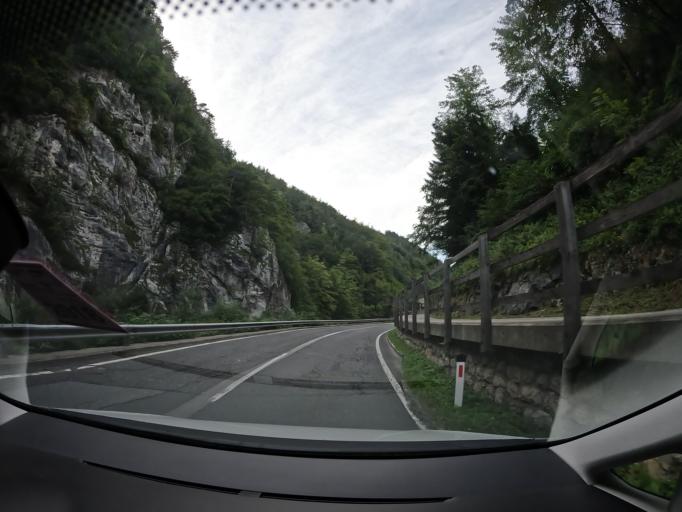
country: AT
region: Carinthia
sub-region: Politischer Bezirk Volkermarkt
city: Bad Eisenkappel
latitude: 46.4986
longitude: 14.5837
